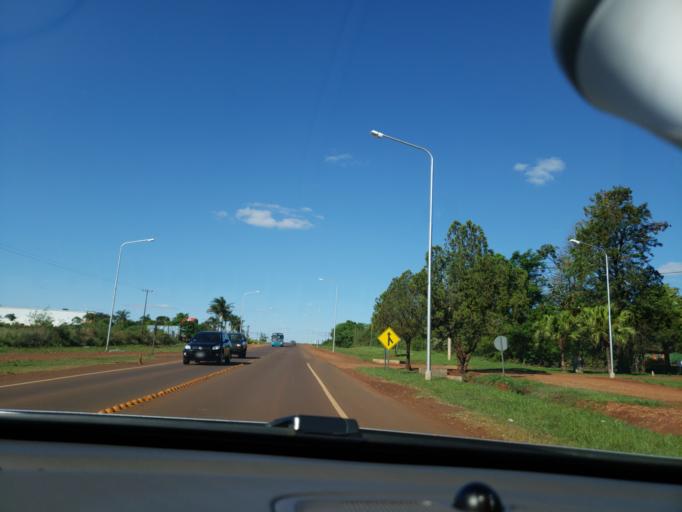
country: AR
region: Misiones
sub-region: Departamento de Capital
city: Posadas
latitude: -27.4096
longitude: -55.9773
